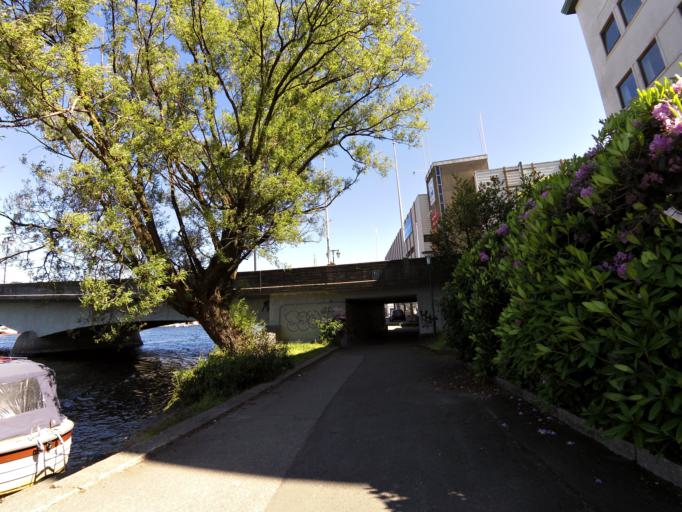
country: NO
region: Vest-Agder
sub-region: Kristiansand
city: Kristiansand
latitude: 58.1493
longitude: 8.0041
